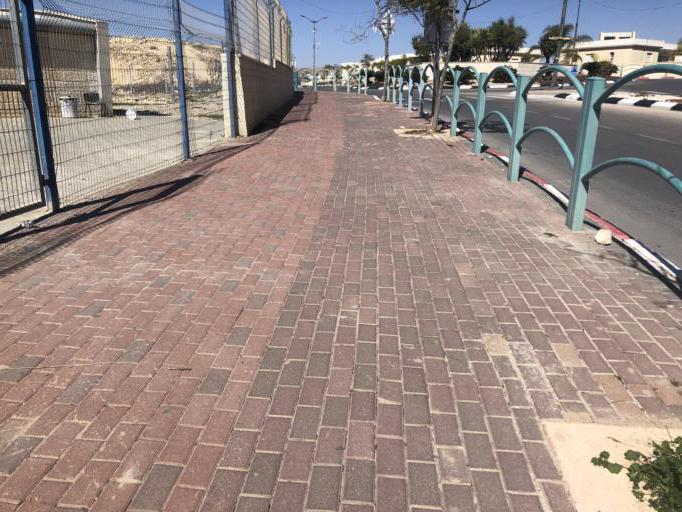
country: IL
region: Southern District
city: Dimona
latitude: 31.0680
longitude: 35.0398
